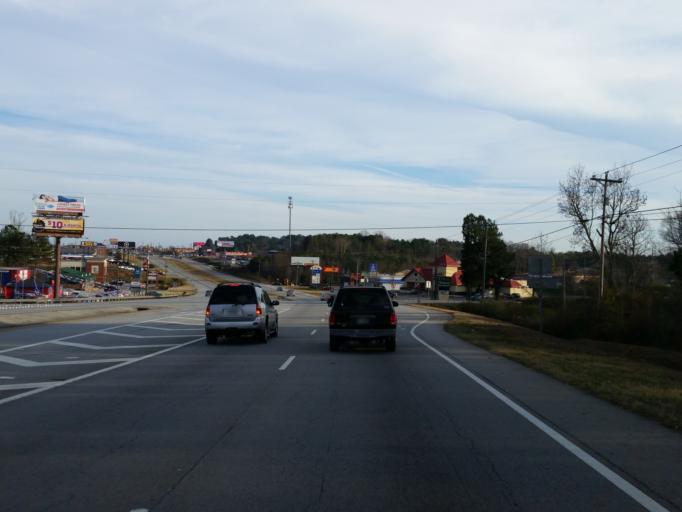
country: US
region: Georgia
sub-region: Paulding County
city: Hiram
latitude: 33.8967
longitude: -84.7669
